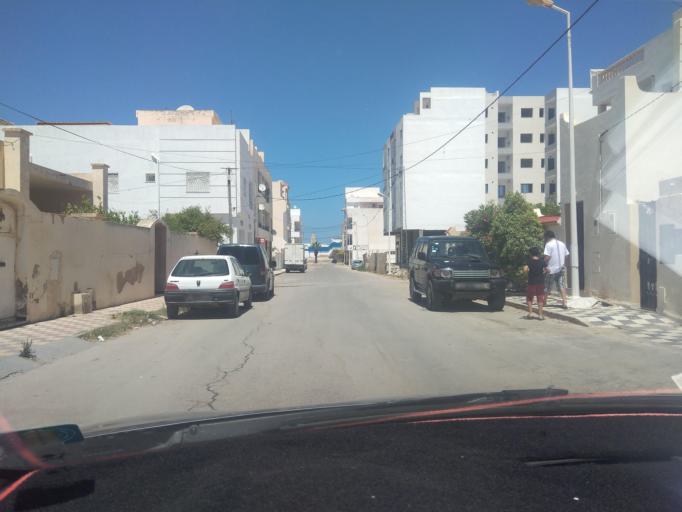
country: TN
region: Susah
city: Hammam Sousse
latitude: 35.8498
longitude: 10.5936
